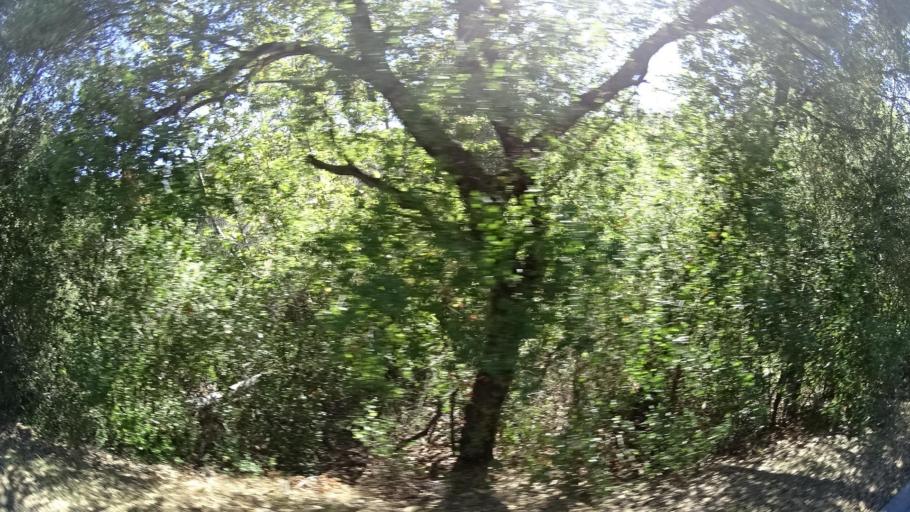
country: US
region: California
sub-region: San Diego County
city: Alpine
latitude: 32.8576
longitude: -116.7745
